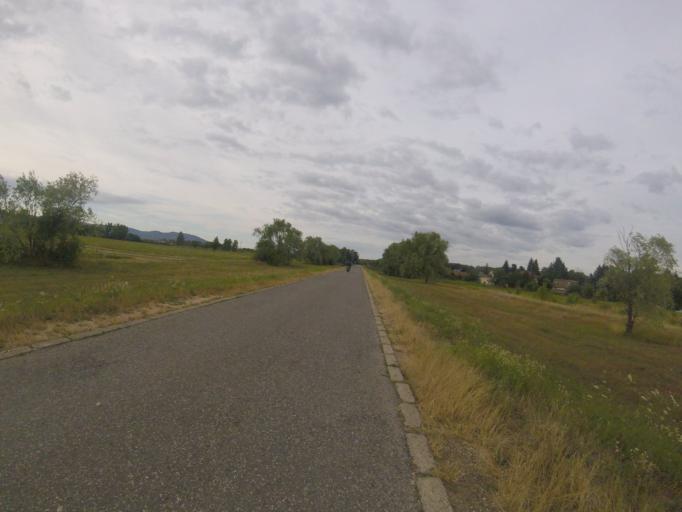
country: HU
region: Pest
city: Budakalasz
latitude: 47.6161
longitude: 19.0782
